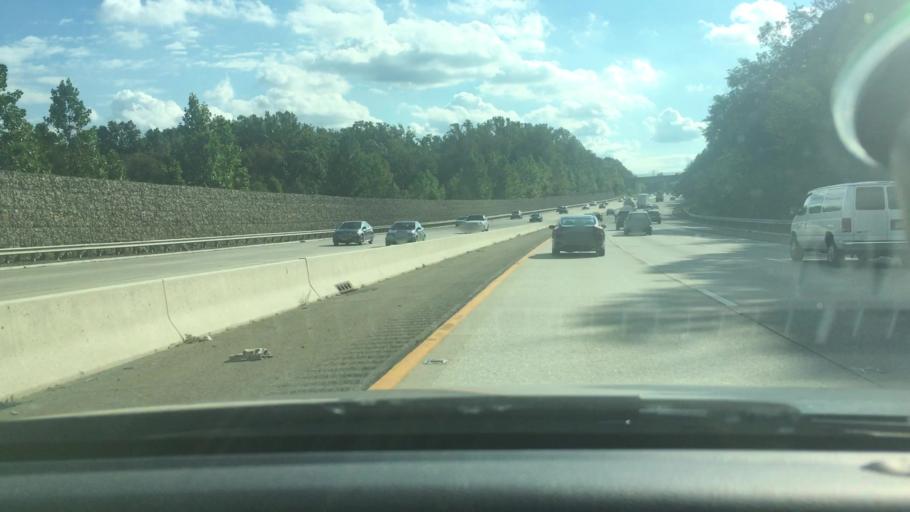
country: US
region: New Jersey
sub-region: Morris County
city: Lincoln Park
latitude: 40.9380
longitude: -74.3502
